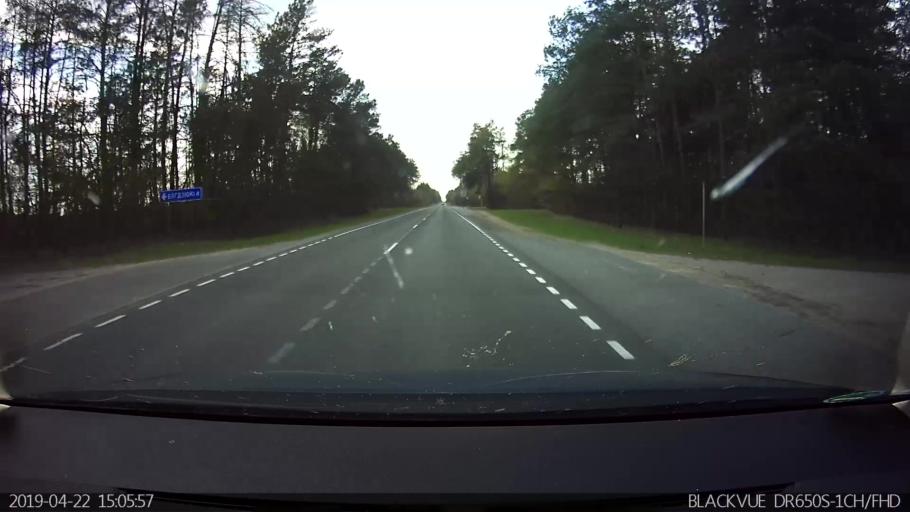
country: BY
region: Brest
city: Kamyanyets
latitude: 52.3329
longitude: 23.8517
